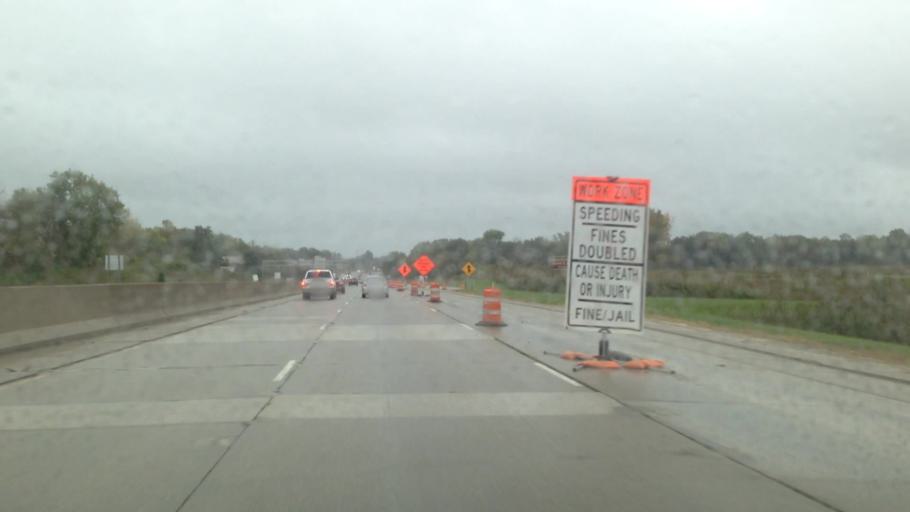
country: US
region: Ohio
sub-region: Summit County
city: Silver Lake
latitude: 41.2011
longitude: -81.4824
